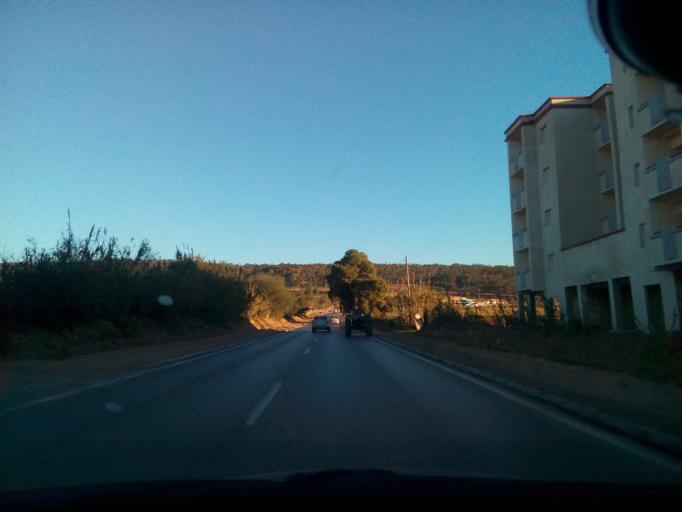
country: DZ
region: Mostaganem
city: Mostaganem
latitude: 35.7743
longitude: 0.1985
